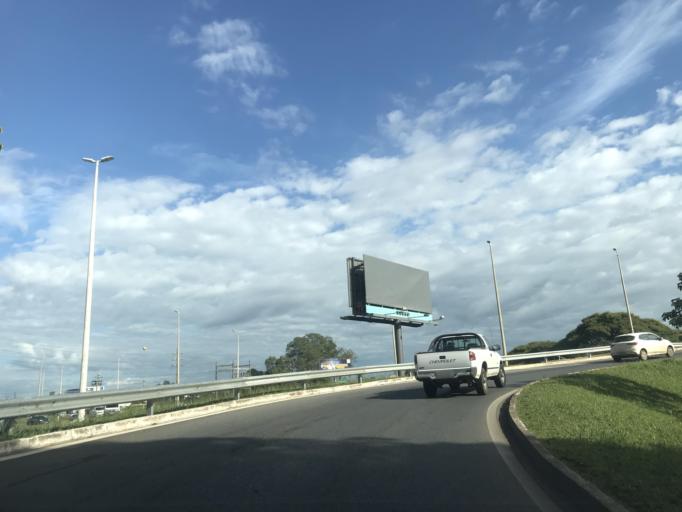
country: BR
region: Federal District
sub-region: Brasilia
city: Brasilia
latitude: -15.8124
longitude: -47.9513
